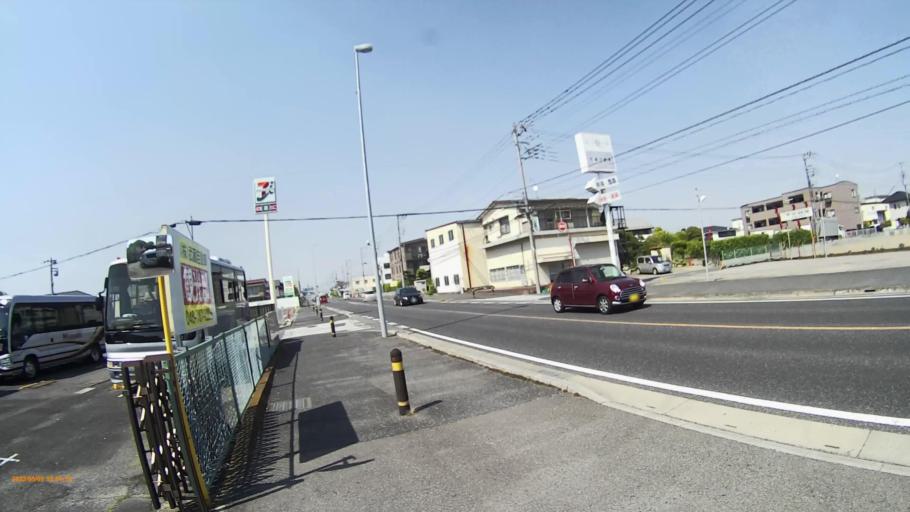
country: JP
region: Saitama
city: Kasukabe
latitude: 35.9953
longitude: 139.7521
